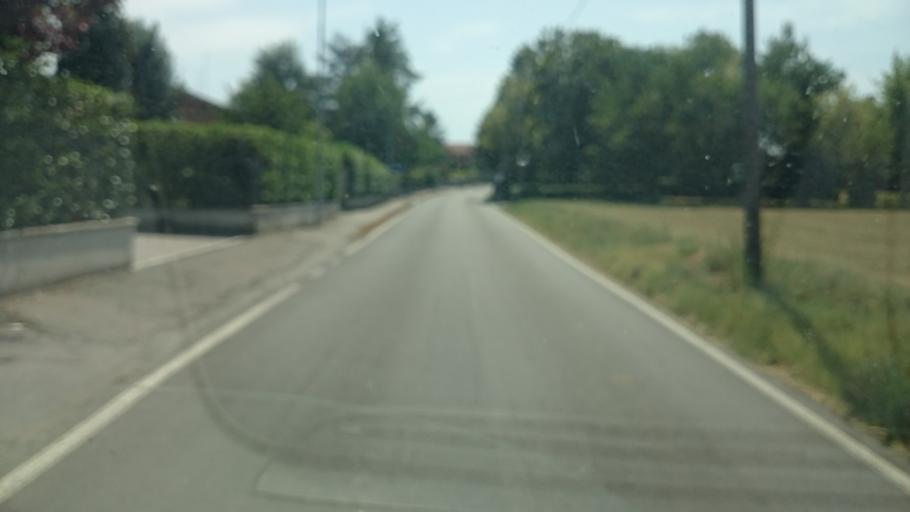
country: IT
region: Emilia-Romagna
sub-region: Provincia di Reggio Emilia
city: Fogliano
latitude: 44.6329
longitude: 10.6654
